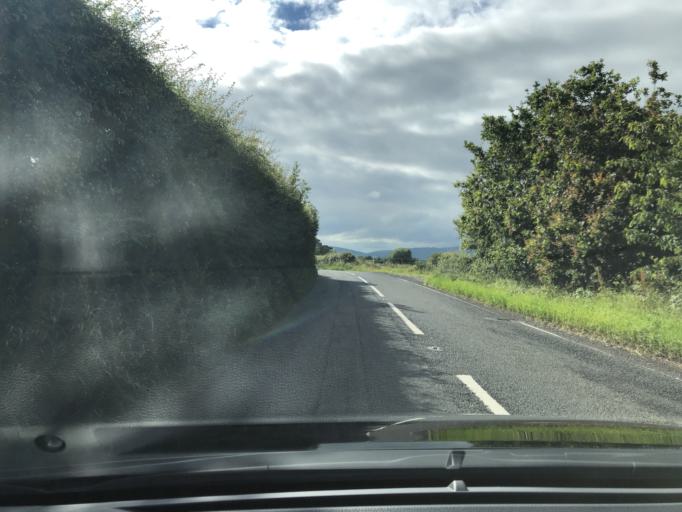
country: GB
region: Northern Ireland
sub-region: Down District
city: Dundrum
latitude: 54.2775
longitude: -5.8008
